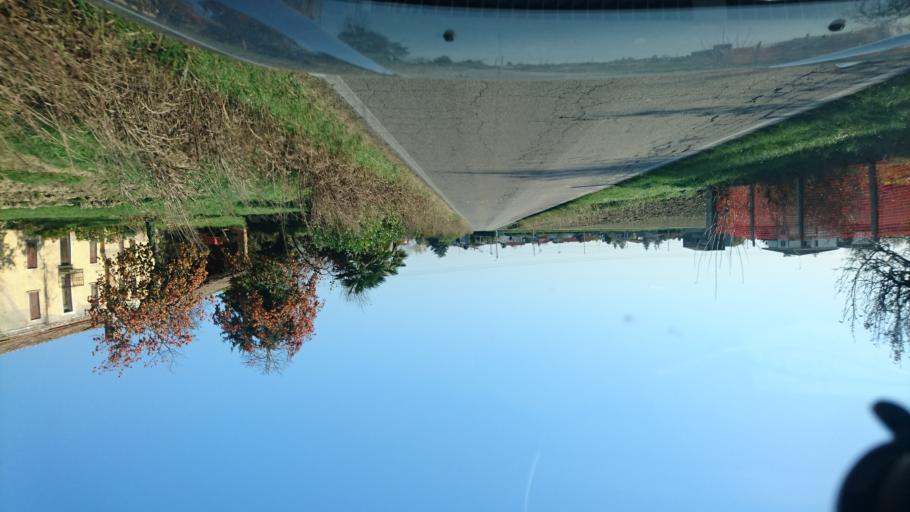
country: IT
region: Veneto
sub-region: Provincia di Padova
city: Ospedaletto Euganeo
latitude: 45.2130
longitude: 11.5914
